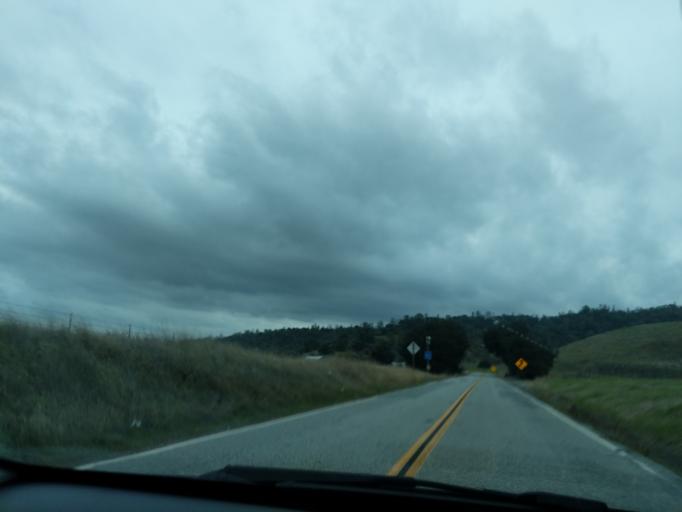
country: US
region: California
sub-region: Monterey County
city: Soledad
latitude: 36.5710
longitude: -121.1841
